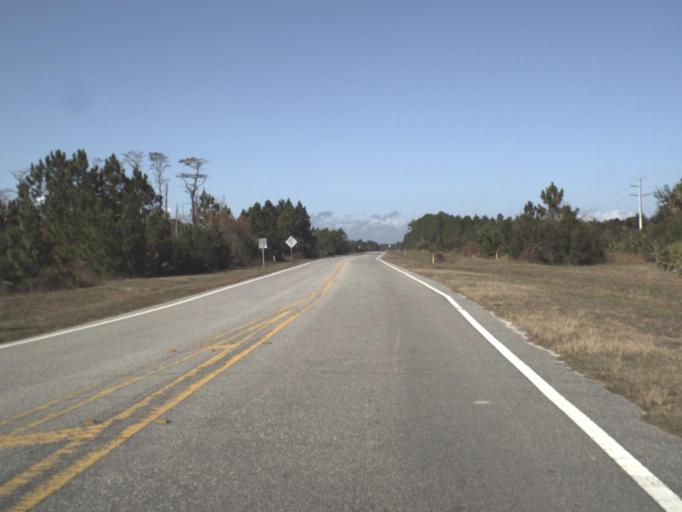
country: US
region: Florida
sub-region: Flagler County
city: Palm Coast
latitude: 29.6047
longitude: -81.2354
